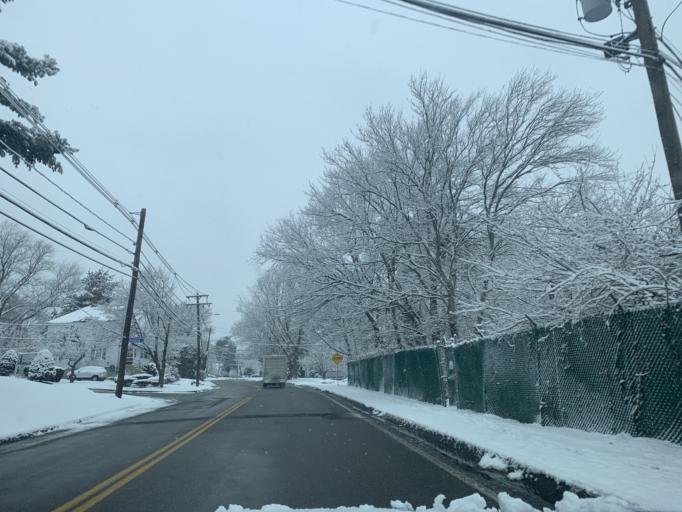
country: US
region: Massachusetts
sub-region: Norfolk County
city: Norwood
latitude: 42.1998
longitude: -71.1893
